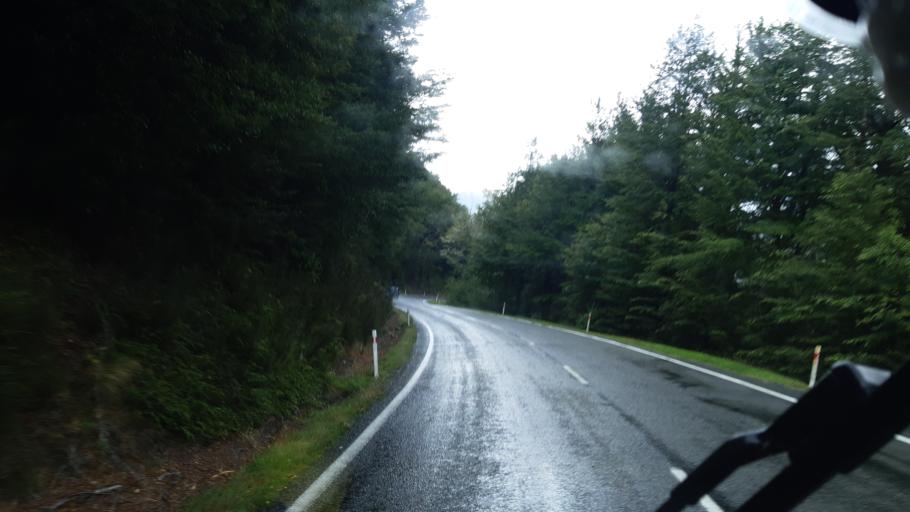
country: NZ
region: Canterbury
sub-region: Hurunui District
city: Amberley
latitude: -42.3748
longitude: 172.3661
